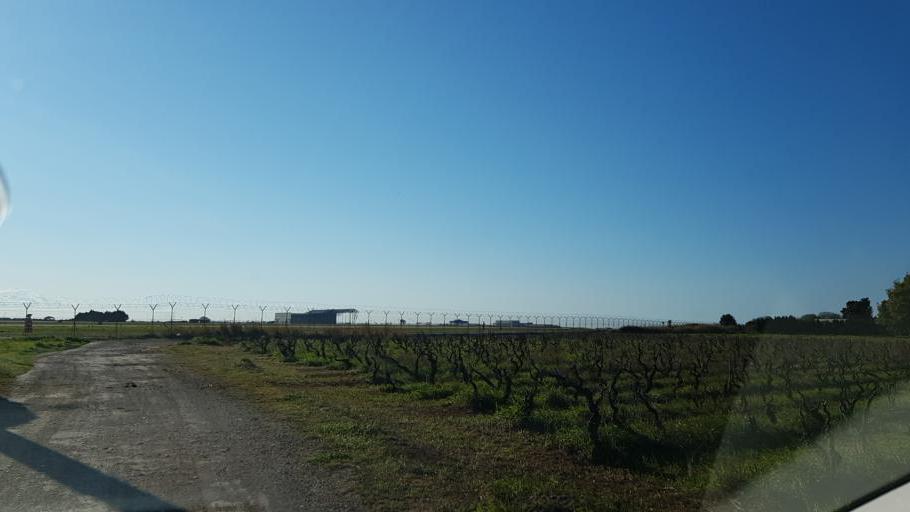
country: IT
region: Apulia
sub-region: Provincia di Brindisi
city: Materdomini
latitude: 40.6689
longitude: 17.9389
